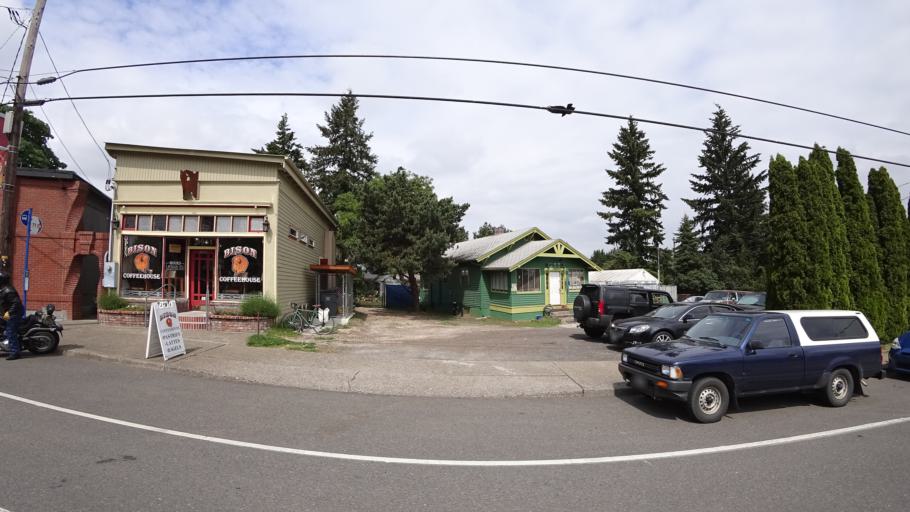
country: US
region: Oregon
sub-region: Multnomah County
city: Portland
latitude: 45.5515
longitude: -122.6050
